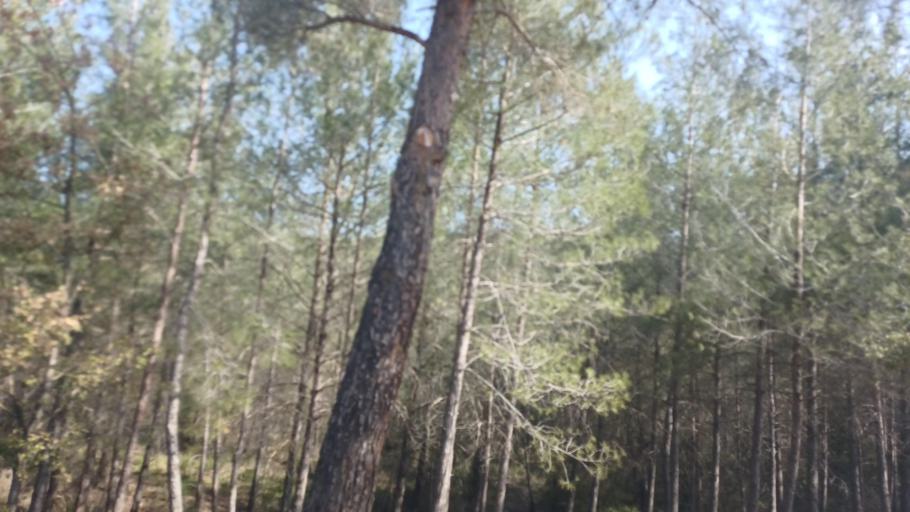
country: CY
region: Limassol
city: Pachna
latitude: 34.8930
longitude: 32.7266
